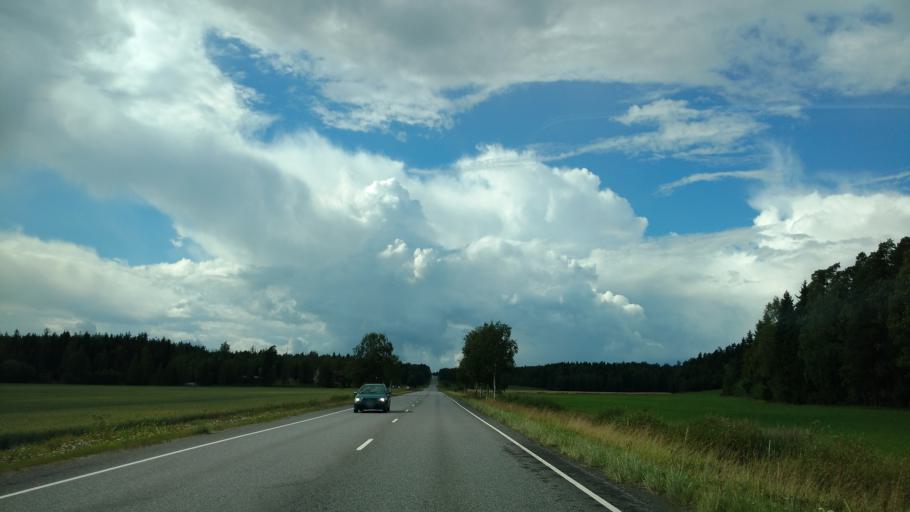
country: FI
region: Varsinais-Suomi
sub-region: Turku
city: Sauvo
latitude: 60.3951
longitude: 22.8544
